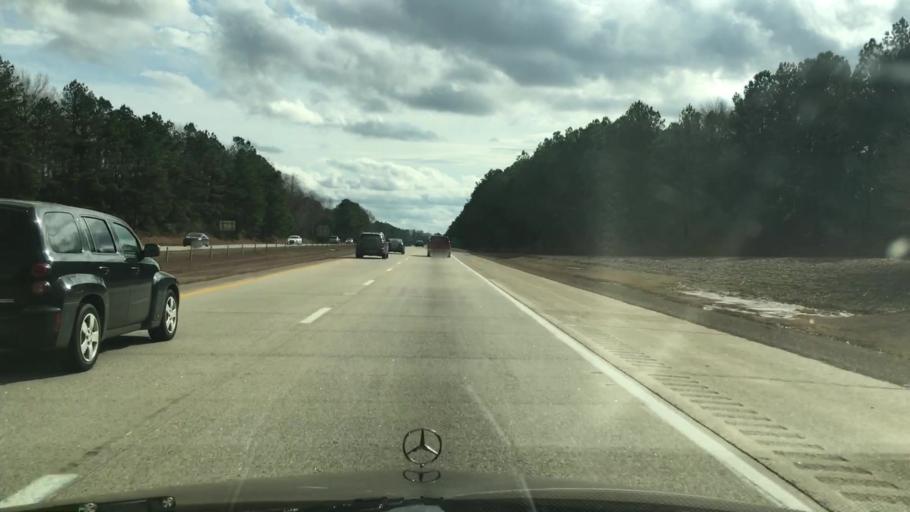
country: US
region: North Carolina
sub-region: Johnston County
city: Benson
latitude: 35.4217
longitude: -78.5297
